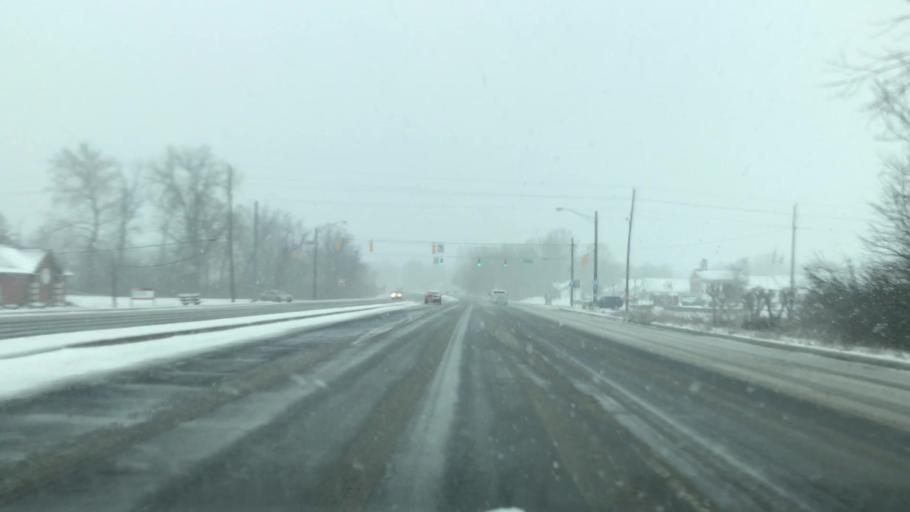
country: US
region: Indiana
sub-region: Marion County
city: Southport
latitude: 39.6727
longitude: -86.1493
